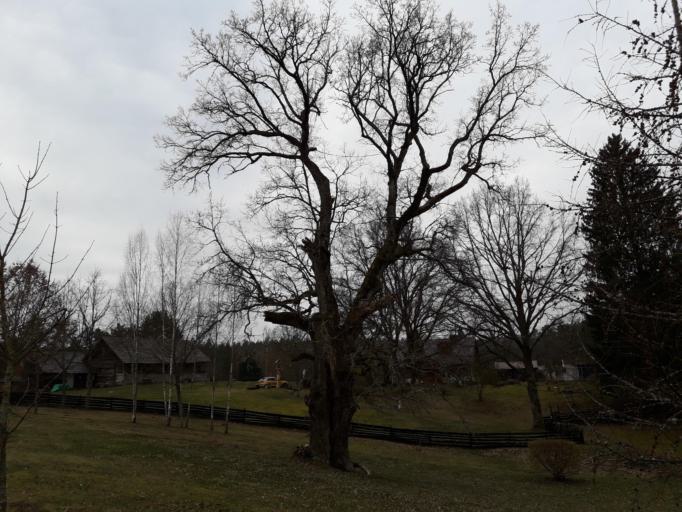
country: LT
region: Alytaus apskritis
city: Druskininkai
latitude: 54.1844
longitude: 24.0825
